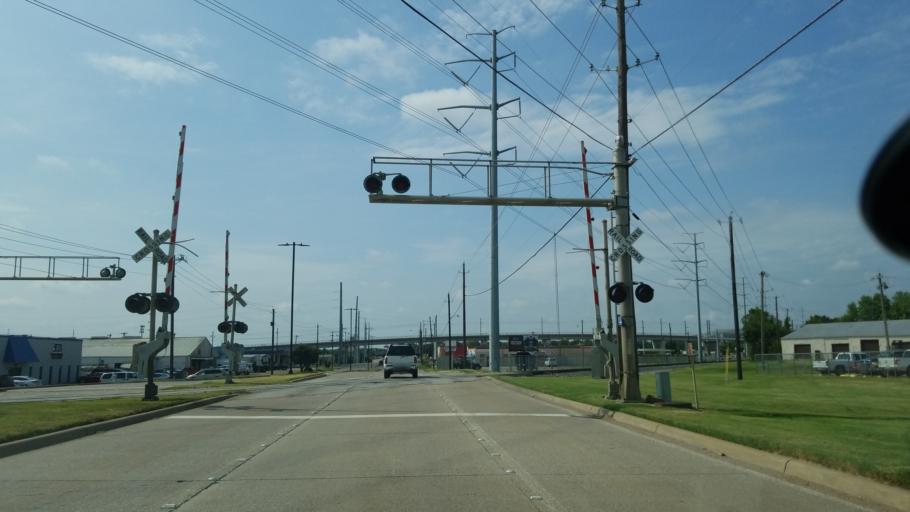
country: US
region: Texas
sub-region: Dallas County
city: Garland
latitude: 32.9196
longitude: -96.6308
